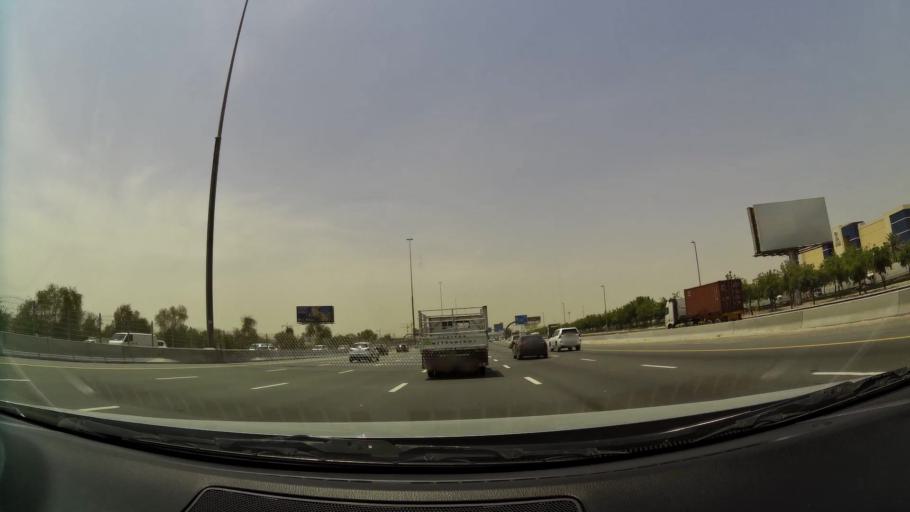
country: AE
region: Ash Shariqah
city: Sharjah
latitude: 25.1728
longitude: 55.3954
